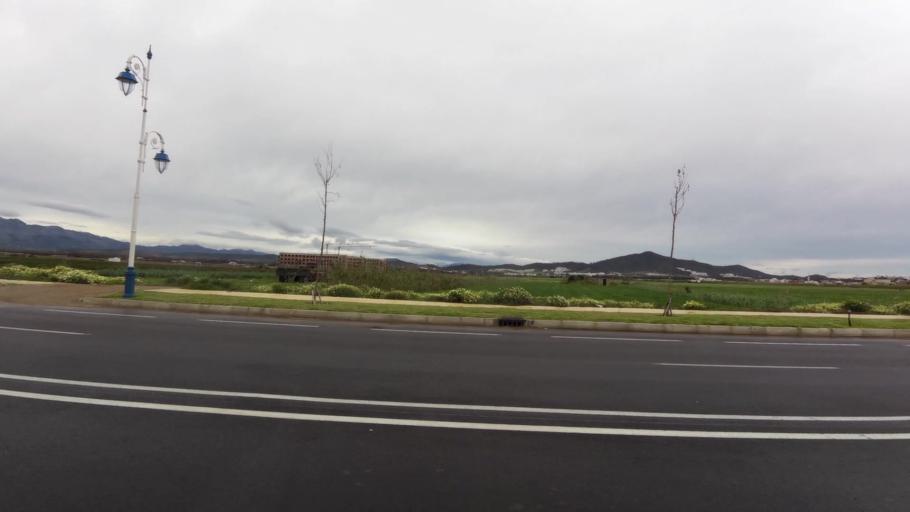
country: MA
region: Tanger-Tetouan
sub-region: Tetouan
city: Martil
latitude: 35.6276
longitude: -5.3005
